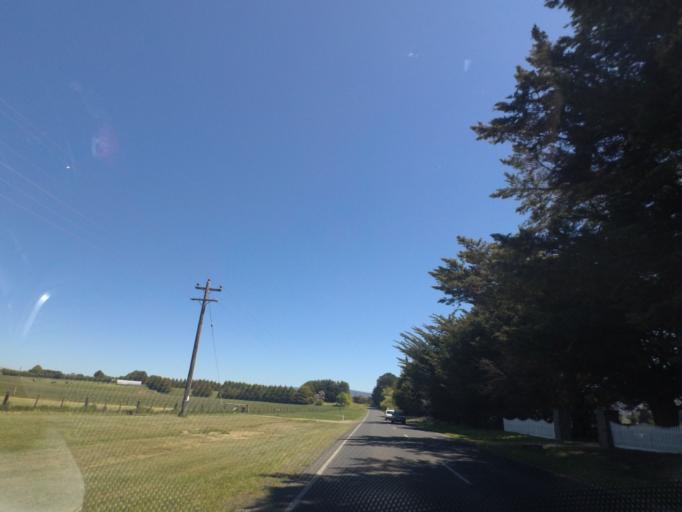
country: AU
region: Victoria
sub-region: Hume
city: Sunbury
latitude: -37.2805
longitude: 144.7495
